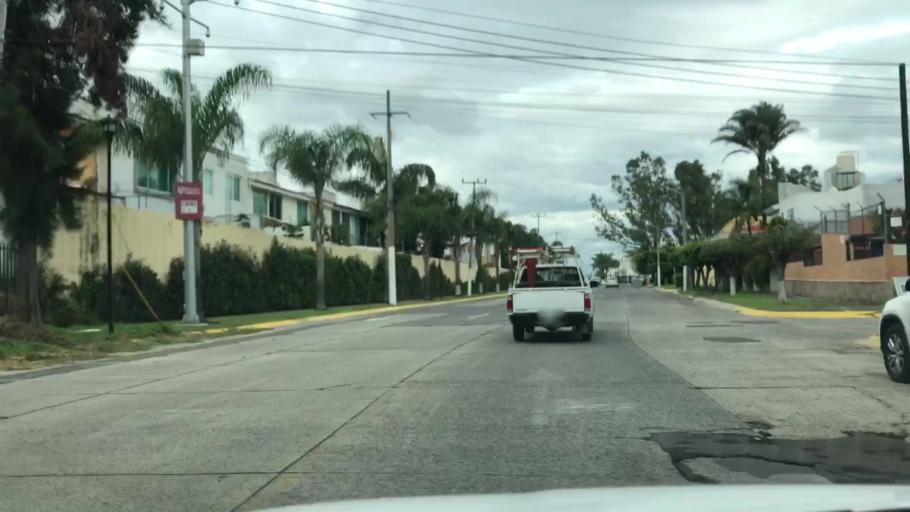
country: MX
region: Jalisco
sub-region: Tlajomulco de Zuniga
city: Palomar
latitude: 20.6401
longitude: -103.4382
